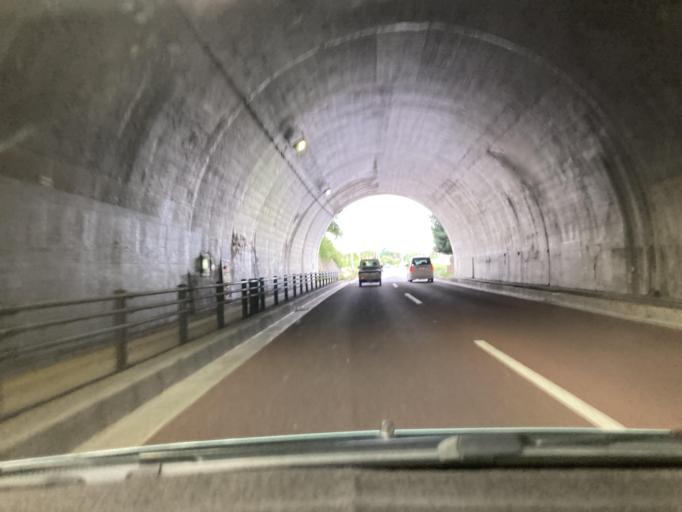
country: JP
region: Okinawa
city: Ginowan
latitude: 26.2549
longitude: 127.7250
